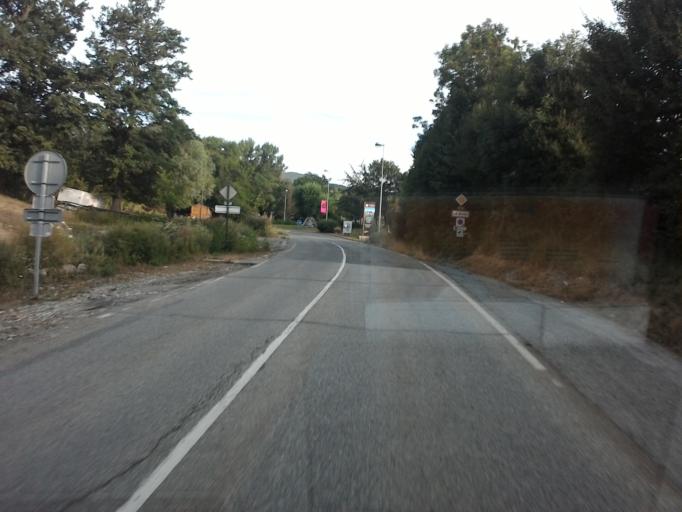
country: FR
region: Rhone-Alpes
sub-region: Departement de l'Isere
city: La Mure
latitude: 44.9011
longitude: 5.8000
